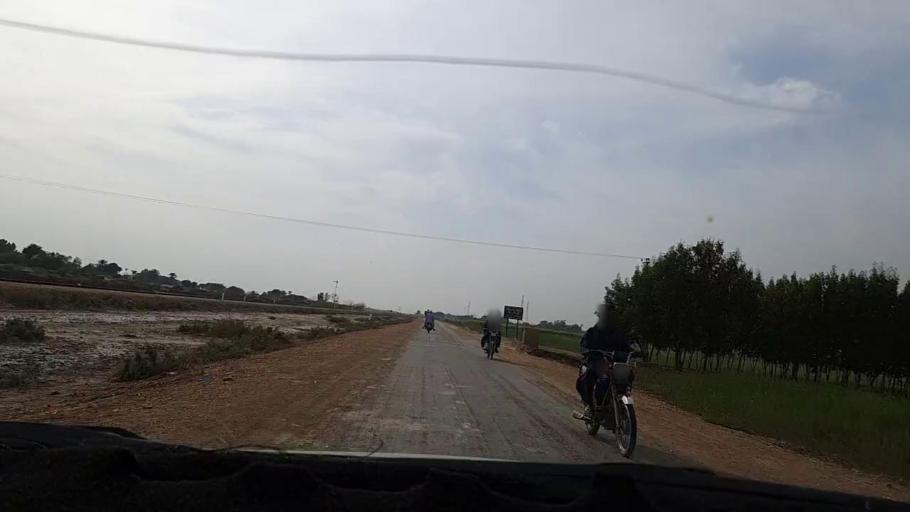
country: PK
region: Sindh
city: Pithoro
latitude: 25.5176
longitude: 69.2481
